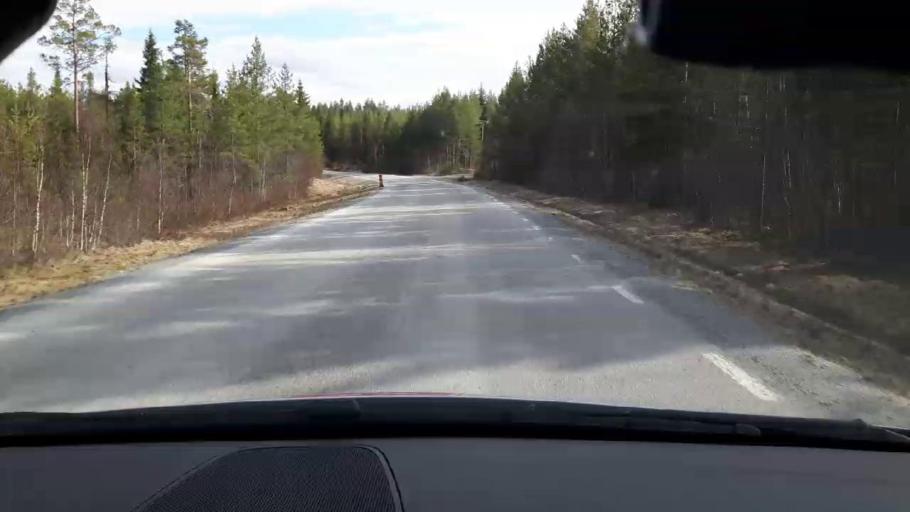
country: SE
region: Jaemtland
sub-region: Bergs Kommun
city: Hoverberg
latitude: 62.7221
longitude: 14.6008
